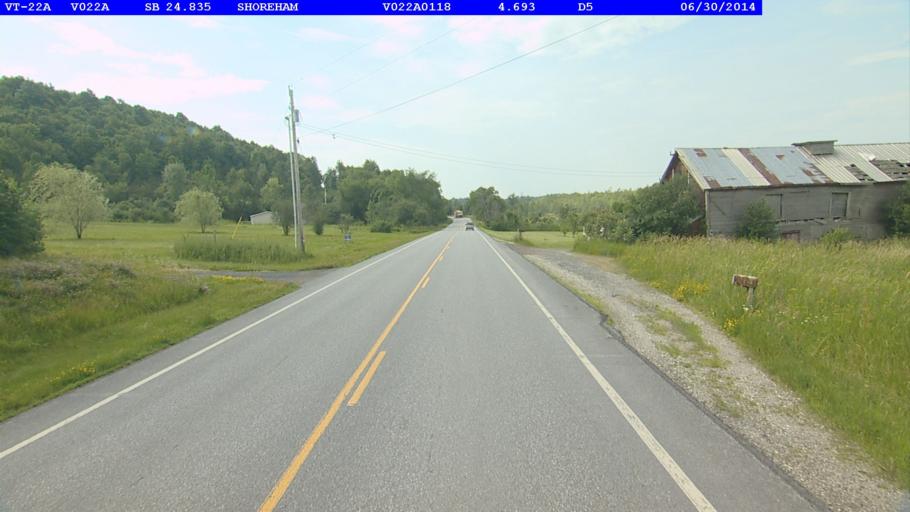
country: US
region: New York
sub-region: Essex County
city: Ticonderoga
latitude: 43.9168
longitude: -73.3124
